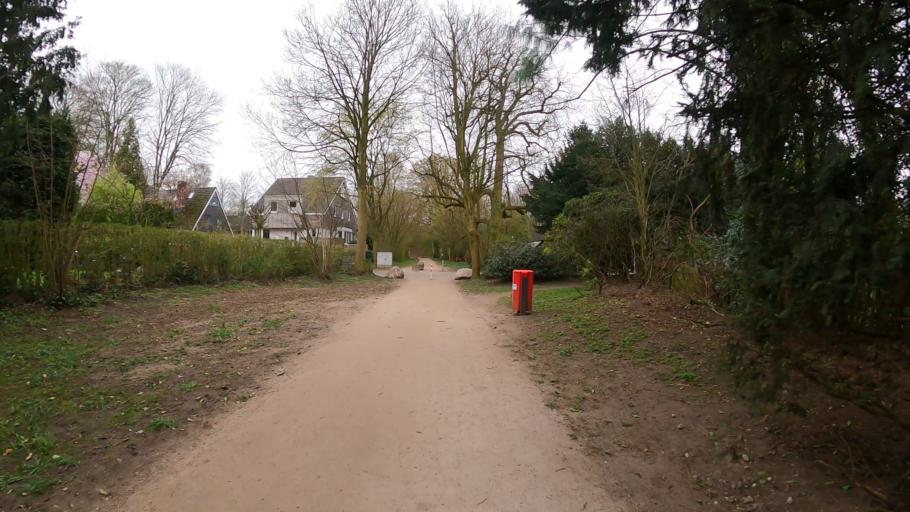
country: DE
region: Hamburg
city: Hamburg-Nord
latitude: 53.6068
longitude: 9.9631
